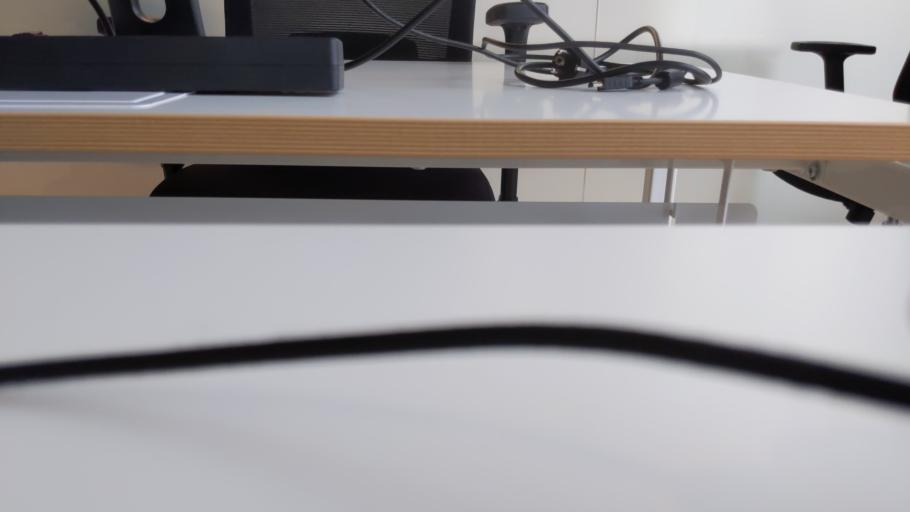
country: RU
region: Moskovskaya
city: Shevlyakovo
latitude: 56.4212
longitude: 36.9800
